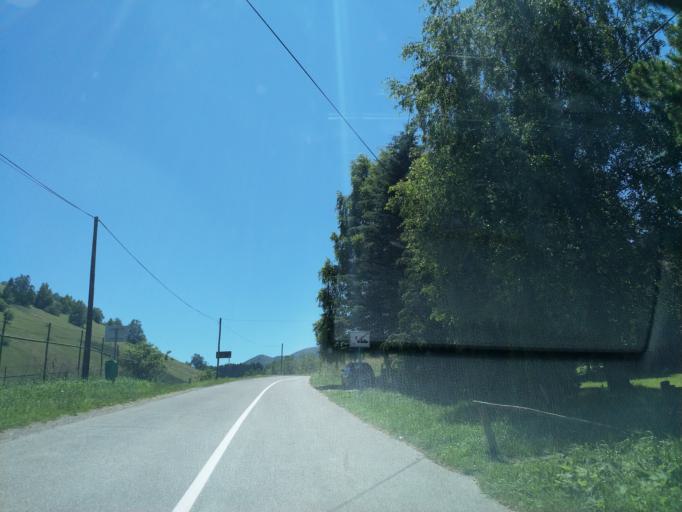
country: XK
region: Mitrovica
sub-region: Komuna e Leposaviqit
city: Leposaviq
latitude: 43.2852
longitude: 20.8785
